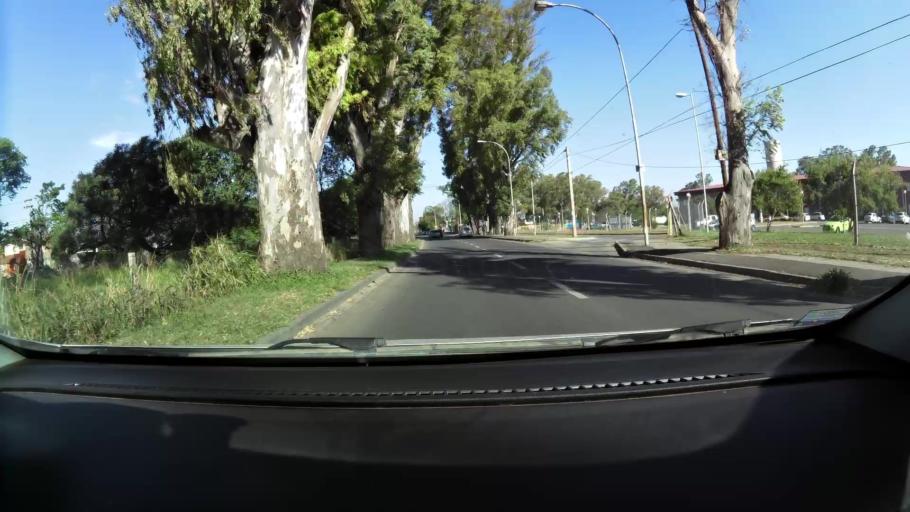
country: AR
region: Cordoba
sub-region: Departamento de Capital
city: Cordoba
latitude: -31.3685
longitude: -64.2138
